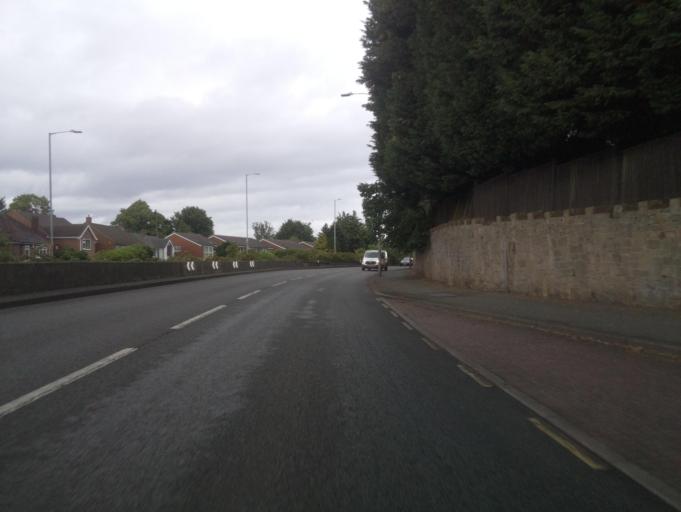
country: GB
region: England
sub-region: Wolverhampton
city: Wolverhampton
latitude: 52.5590
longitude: -2.1622
